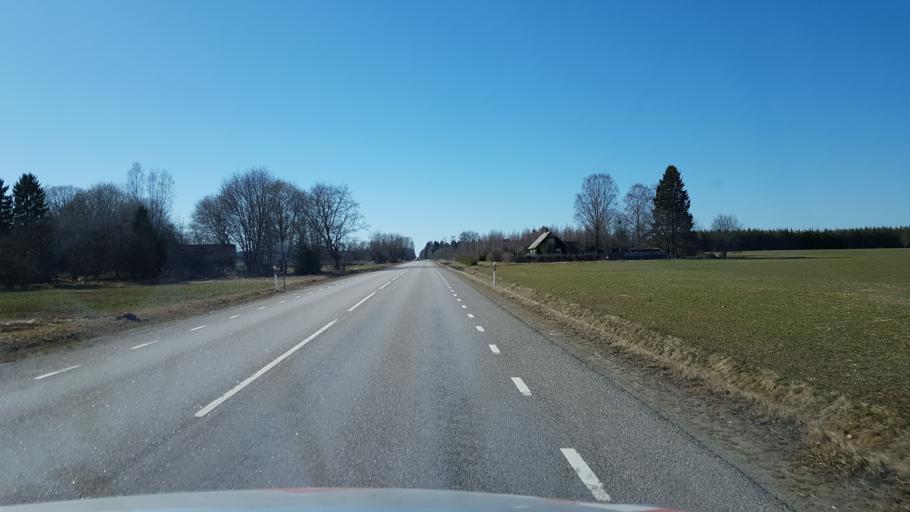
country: EE
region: Laeaene-Virumaa
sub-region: Viru-Nigula vald
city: Kunda
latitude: 59.3537
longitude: 26.6723
